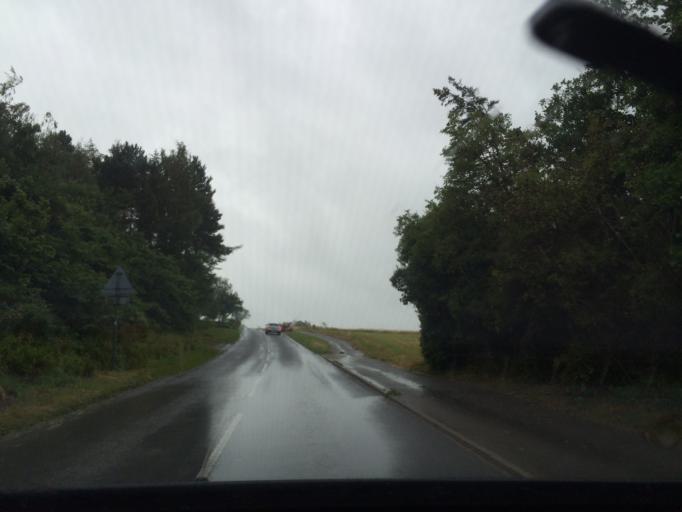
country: DK
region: Zealand
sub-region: Vordingborg Kommune
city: Stege
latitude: 55.0293
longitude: 12.2934
